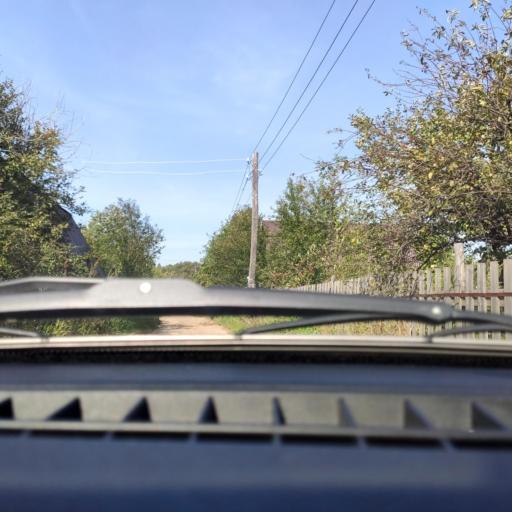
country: RU
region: Bashkortostan
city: Blagoveshchensk
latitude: 54.9428
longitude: 56.0897
